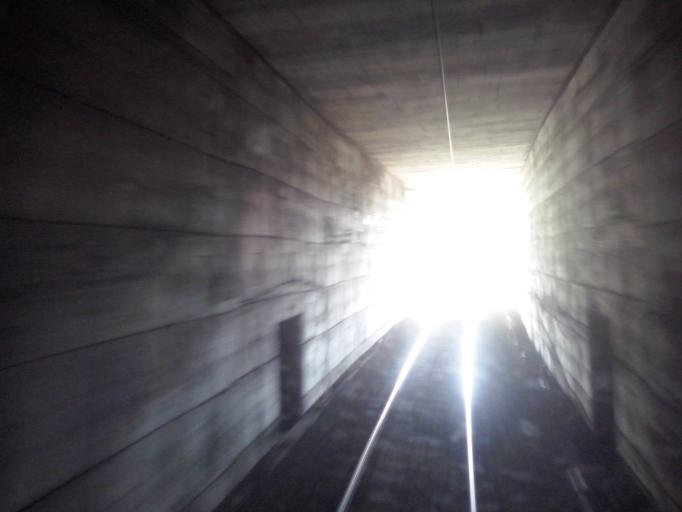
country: RS
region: Central Serbia
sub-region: Zlatiborski Okrug
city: Kosjeric
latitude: 43.9571
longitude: 19.9794
